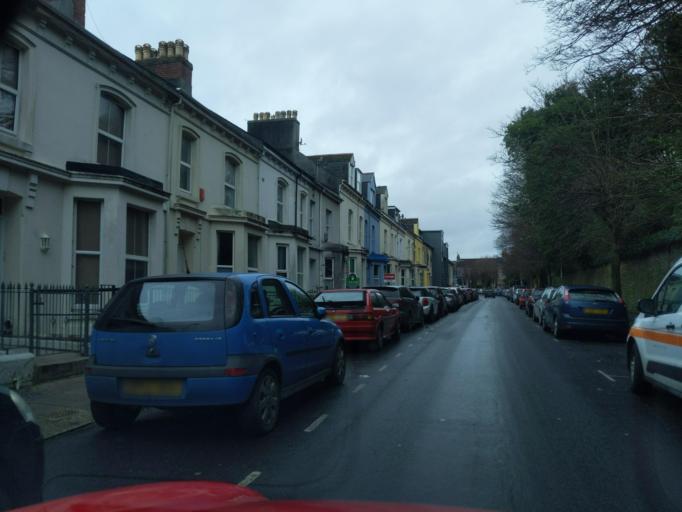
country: GB
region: England
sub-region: Plymouth
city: Plymouth
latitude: 50.3802
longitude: -4.1362
